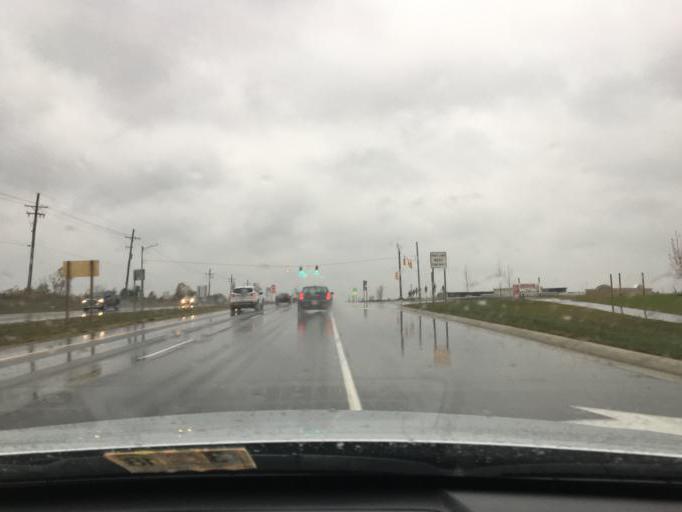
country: US
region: Michigan
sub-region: Oakland County
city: Auburn Hills
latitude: 42.7049
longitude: -83.2424
